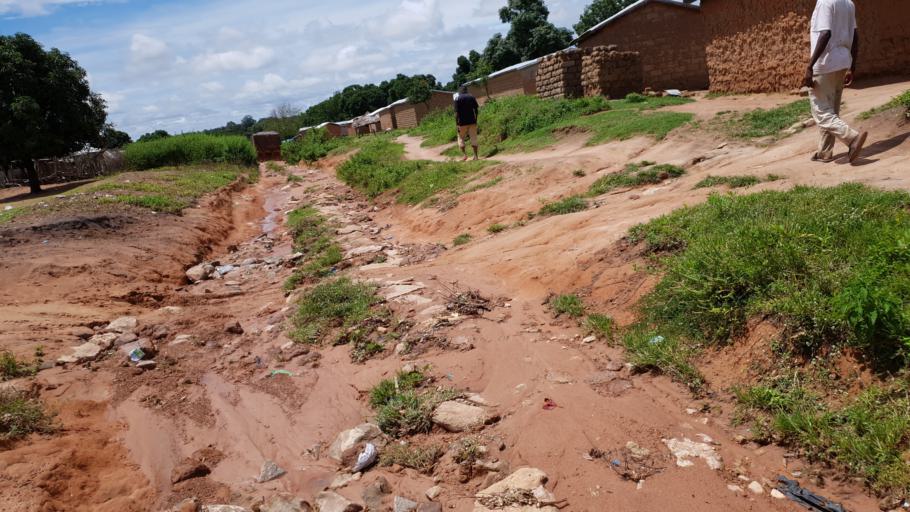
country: CI
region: Savanes
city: Tengrela
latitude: 10.3590
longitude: -6.9189
